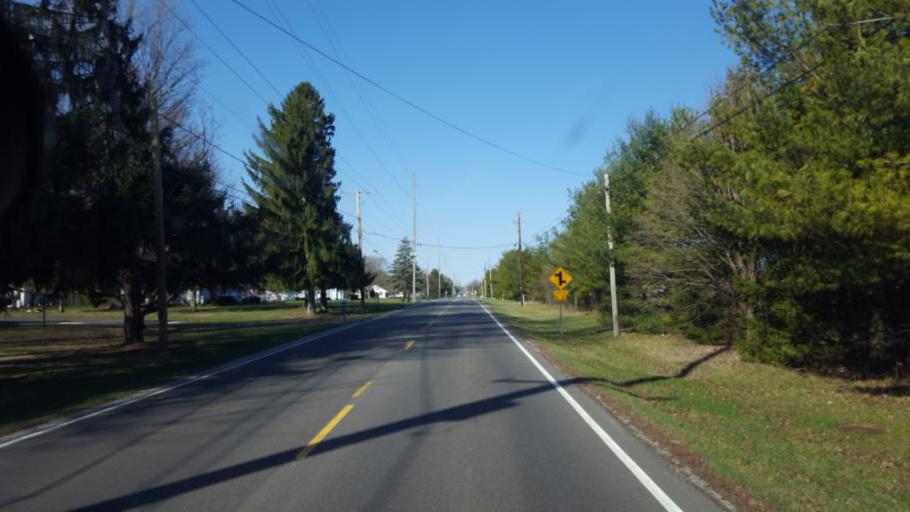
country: US
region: Ohio
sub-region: Marion County
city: Marion
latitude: 40.5641
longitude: -83.0932
